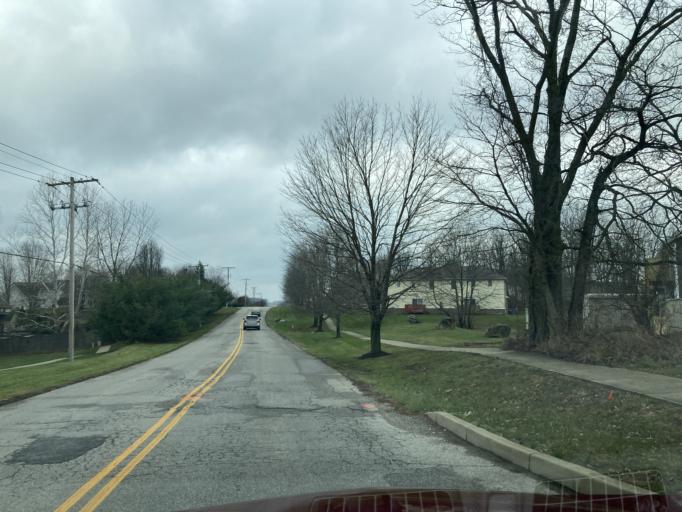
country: US
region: Indiana
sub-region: Monroe County
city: Bloomington
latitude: 39.1218
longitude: -86.5448
